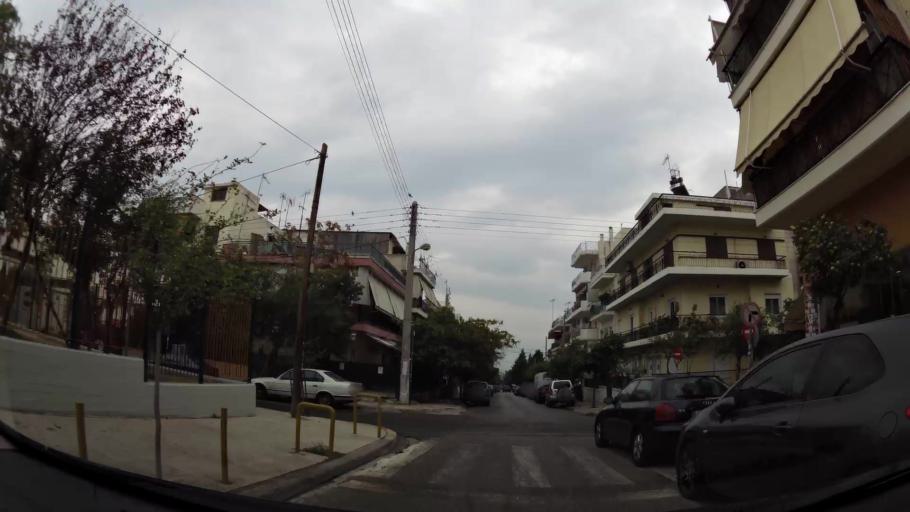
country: GR
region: Attica
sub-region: Nomos Piraios
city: Korydallos
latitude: 37.9828
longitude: 23.6537
